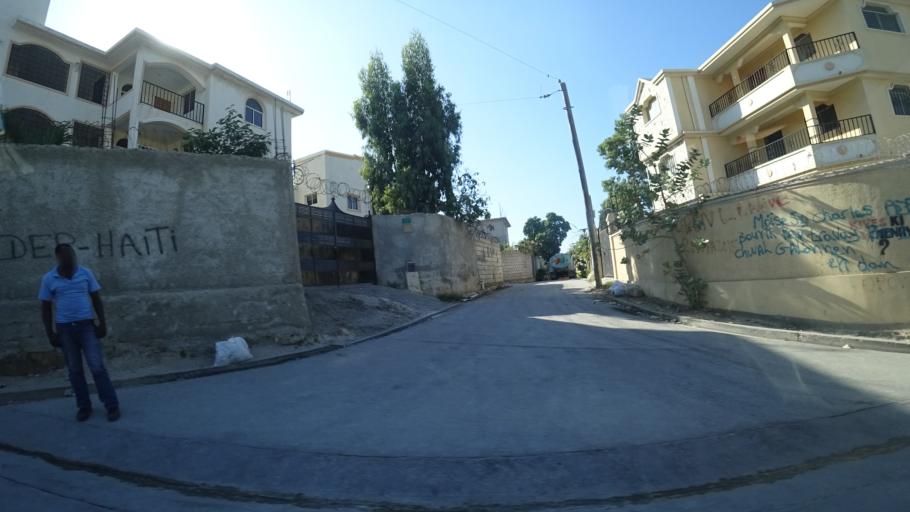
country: HT
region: Ouest
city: Delmas 73
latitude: 18.5432
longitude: -72.2867
